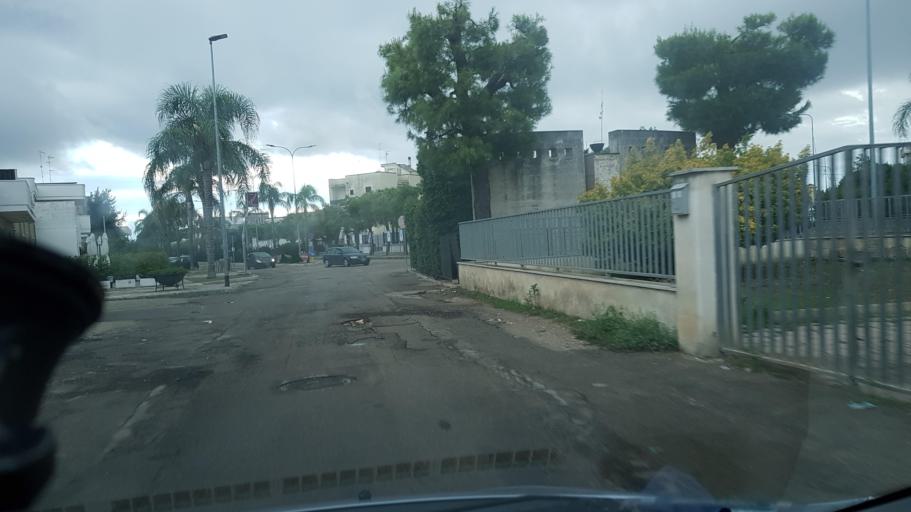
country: IT
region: Apulia
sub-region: Provincia di Lecce
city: Carmiano
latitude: 40.3512
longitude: 18.0375
